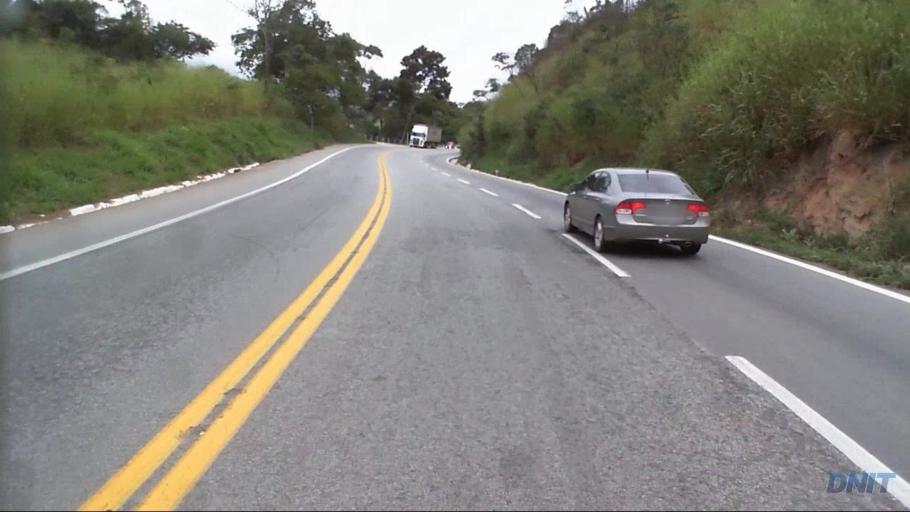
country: BR
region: Minas Gerais
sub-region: Caete
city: Caete
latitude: -19.7511
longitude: -43.6291
